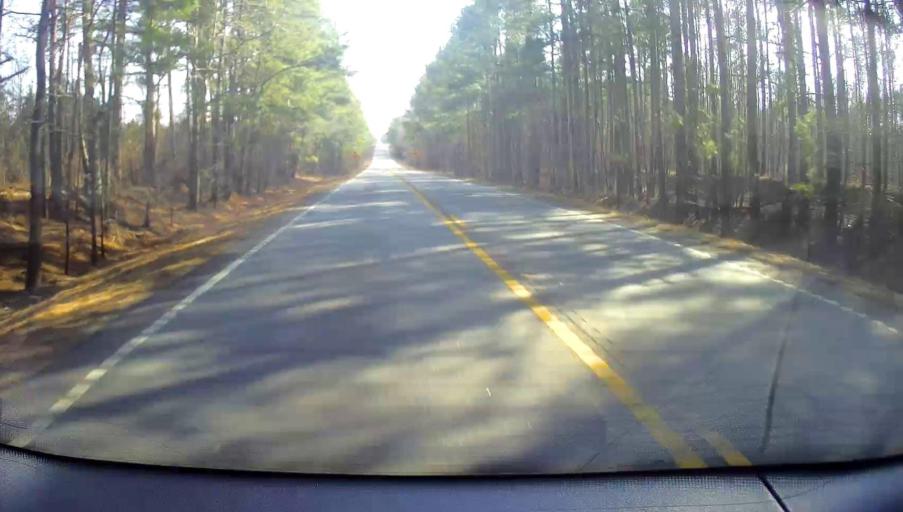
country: US
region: Georgia
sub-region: Butts County
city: Indian Springs
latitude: 33.1557
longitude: -83.8395
